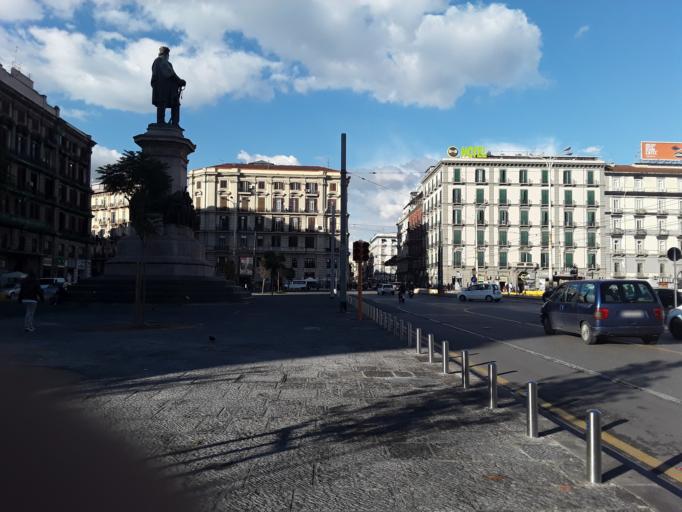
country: IT
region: Campania
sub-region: Provincia di Napoli
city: Napoli
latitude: 40.8519
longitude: 14.2680
